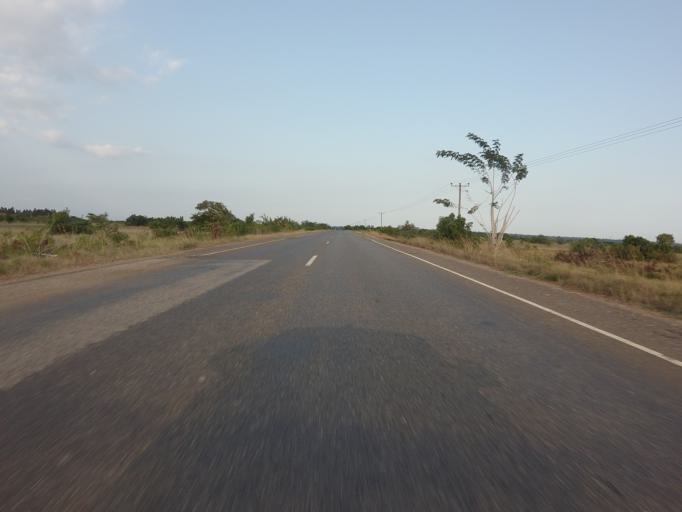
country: GH
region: Volta
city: Anloga
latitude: 6.0802
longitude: 0.5794
